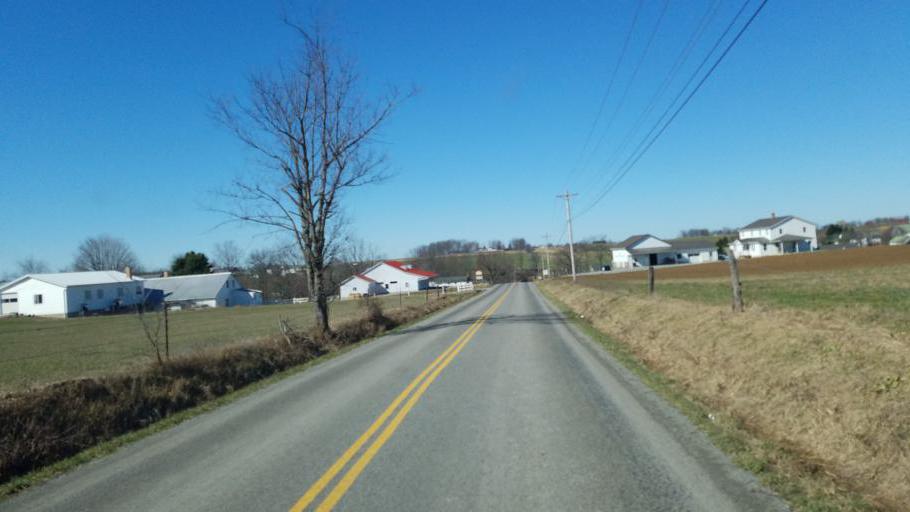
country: US
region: Ohio
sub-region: Wayne County
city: Apple Creek
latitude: 40.6532
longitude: -81.7599
